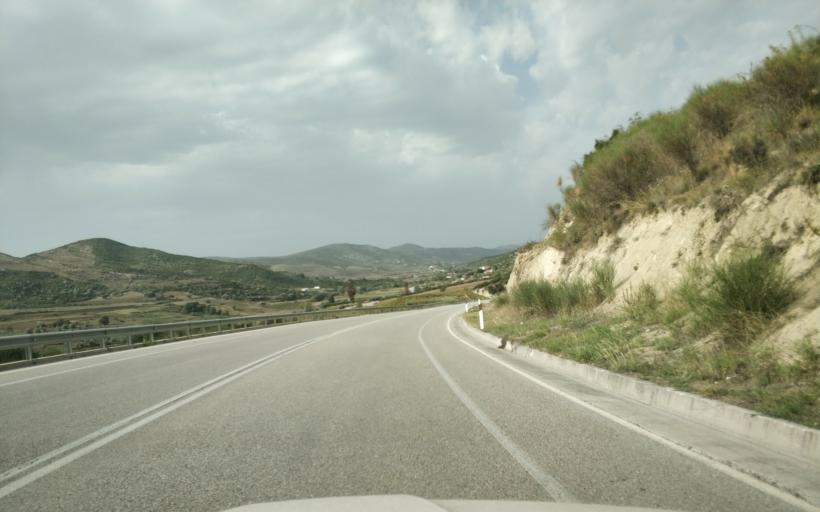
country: AL
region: Gjirokaster
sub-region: Rrethi i Tepelenes
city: Krahes
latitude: 40.3998
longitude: 19.8639
